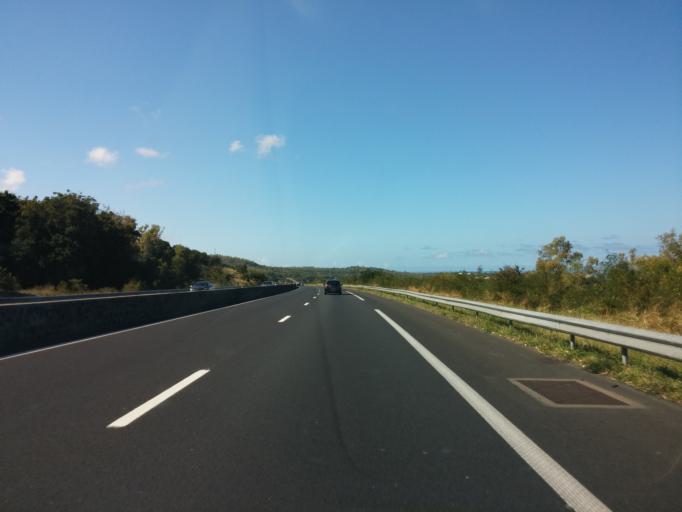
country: RE
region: Reunion
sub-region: Reunion
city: Les Avirons
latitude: -21.2527
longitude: 55.3282
